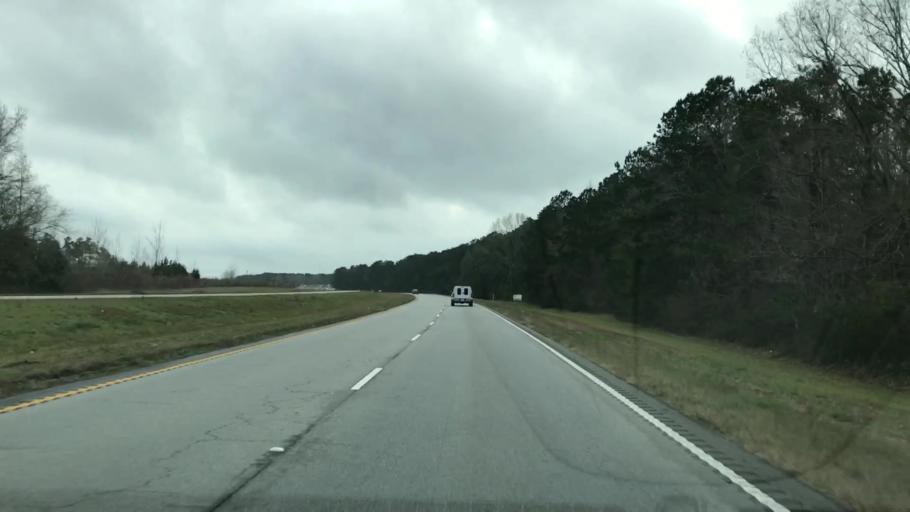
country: US
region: South Carolina
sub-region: Berkeley County
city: Moncks Corner
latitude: 33.1613
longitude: -80.0315
